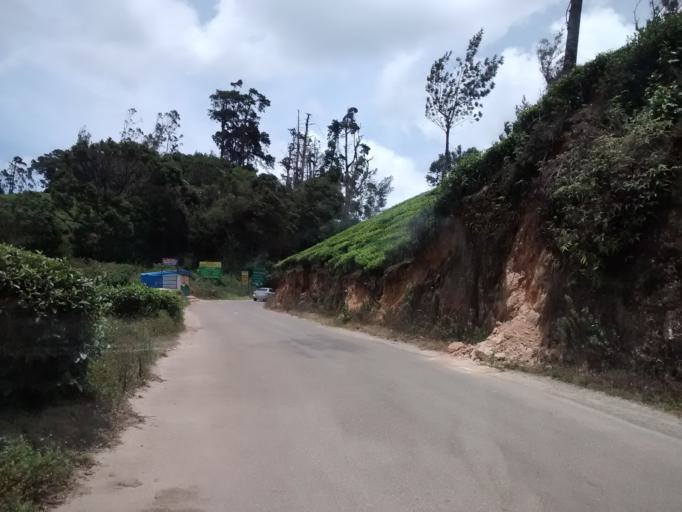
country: IN
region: Tamil Nadu
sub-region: Theni
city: Bodinayakkanur
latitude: 10.1285
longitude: 77.2351
